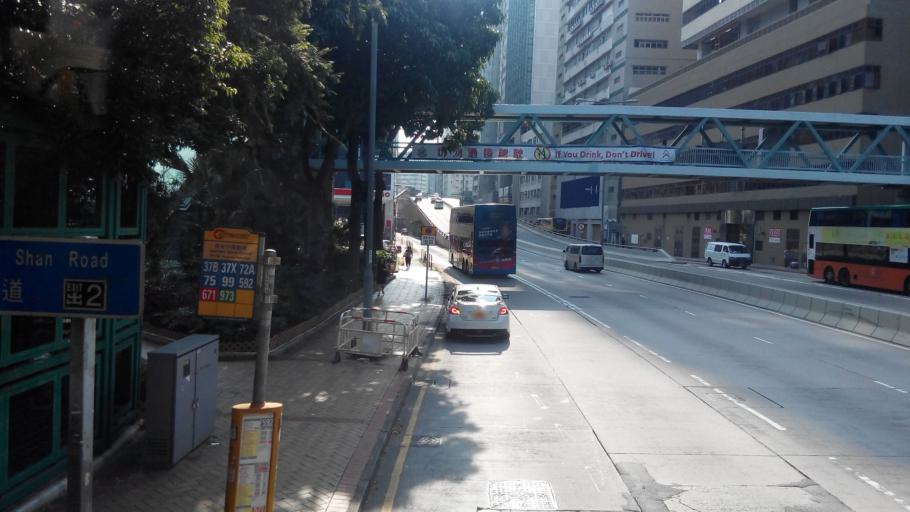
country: HK
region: Wanchai
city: Wan Chai
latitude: 22.2501
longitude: 114.1699
